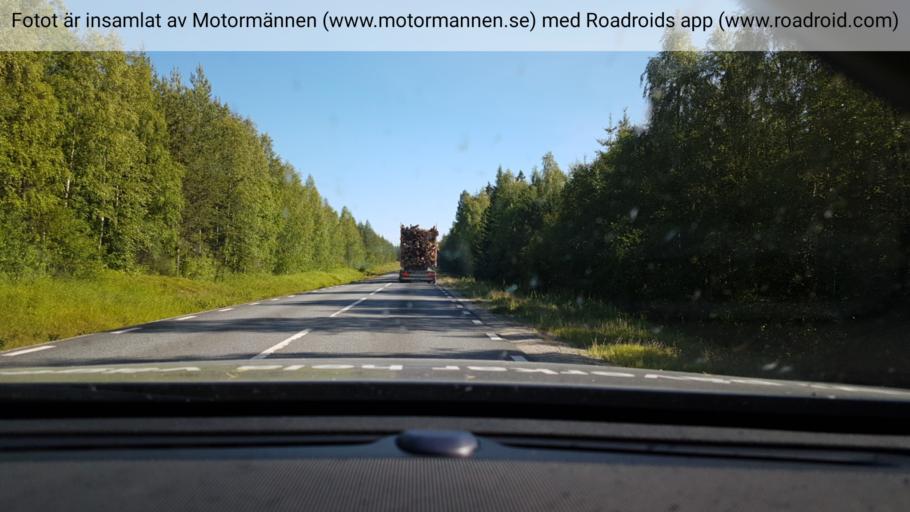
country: SE
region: Vaesterbotten
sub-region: Bjurholms Kommun
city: Bjurholm
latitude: 64.3223
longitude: 19.1576
